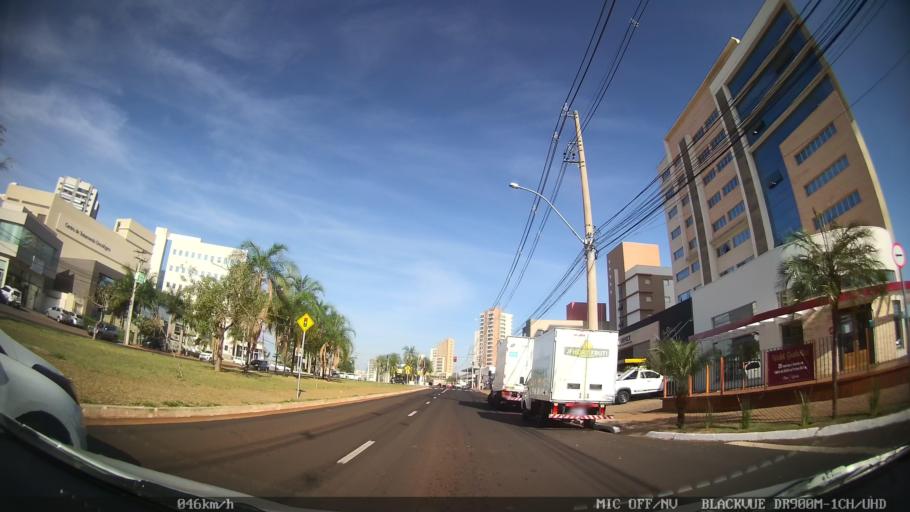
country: BR
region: Sao Paulo
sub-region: Ribeirao Preto
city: Ribeirao Preto
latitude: -21.2164
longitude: -47.8239
